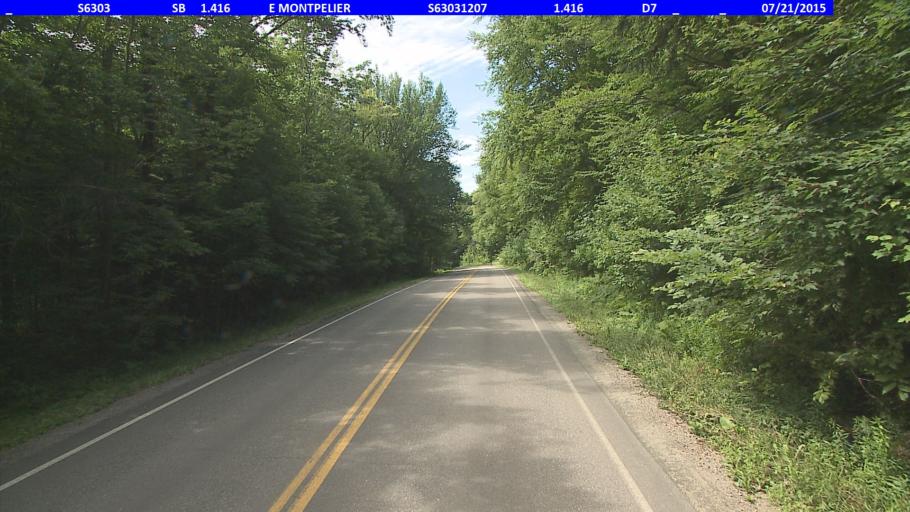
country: US
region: Vermont
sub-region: Washington County
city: Montpelier
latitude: 44.2896
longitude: -72.5415
